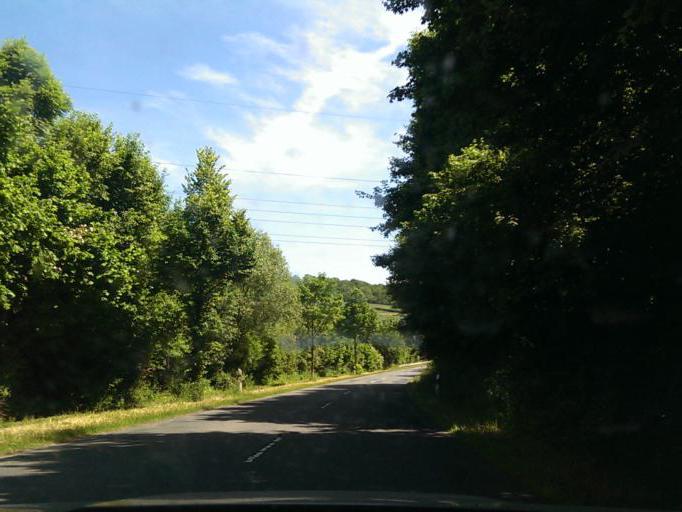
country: DE
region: Lower Saxony
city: Alfeld
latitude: 51.9861
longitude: 9.7809
